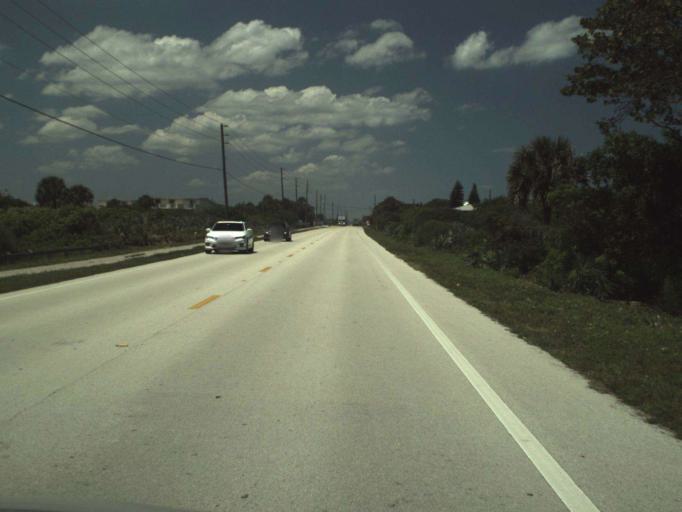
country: US
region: Florida
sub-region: Brevard County
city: Malabar
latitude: 28.0029
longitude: -80.5268
